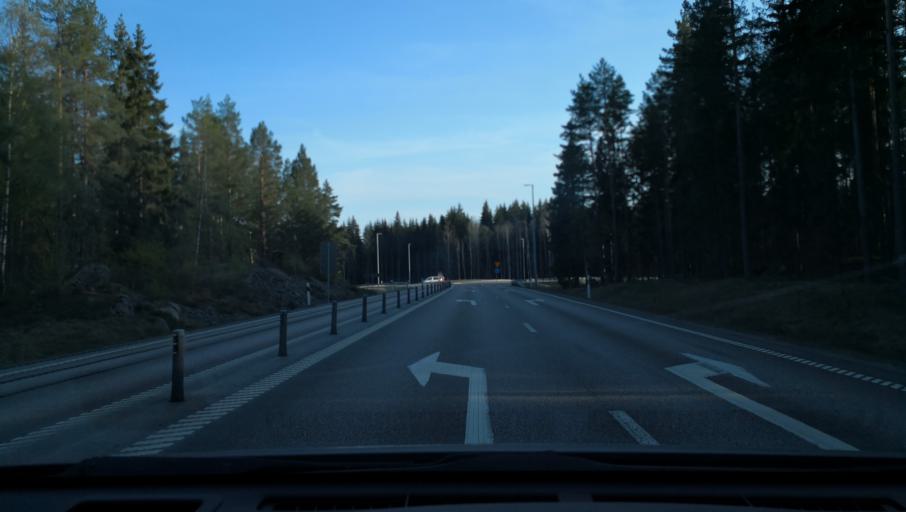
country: SE
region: Uppsala
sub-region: Heby Kommun
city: Heby
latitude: 59.9386
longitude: 16.8289
